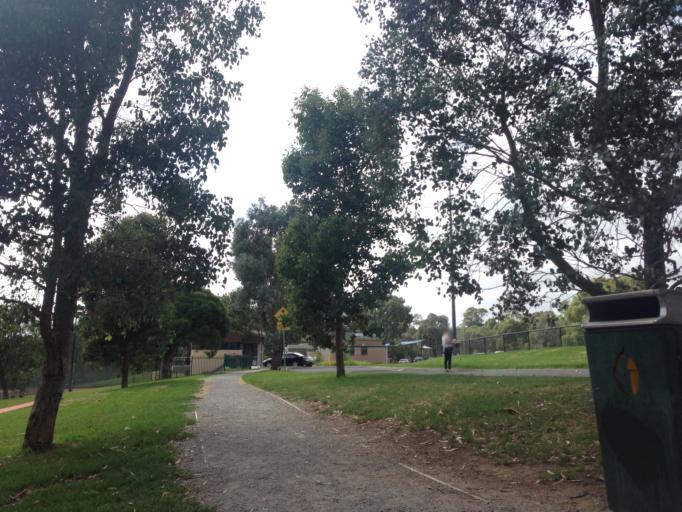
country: AU
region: Victoria
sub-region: Boroondara
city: Balwyn North
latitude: -37.7970
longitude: 145.0929
